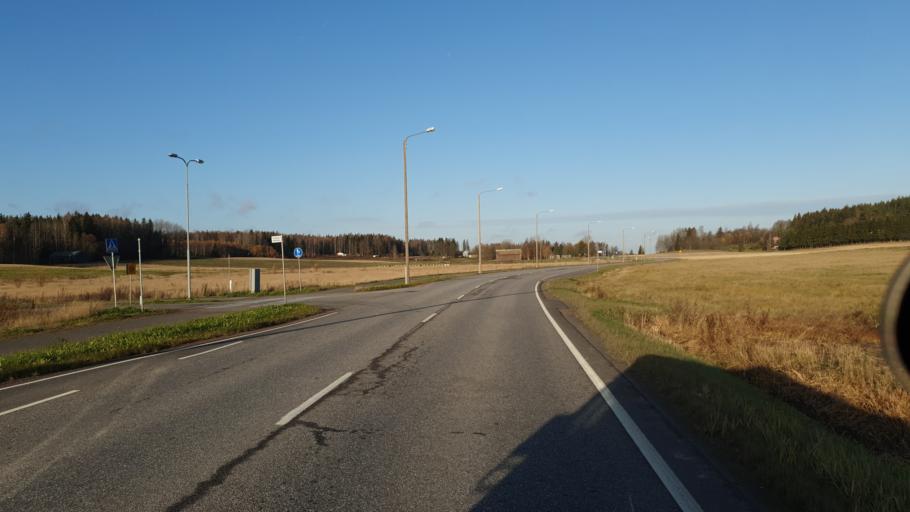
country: FI
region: Uusimaa
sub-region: Helsinki
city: Siuntio
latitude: 60.1473
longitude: 24.2176
